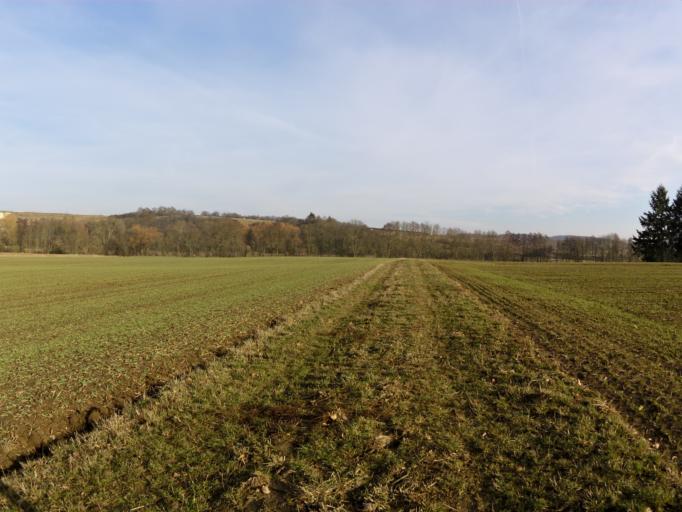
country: DE
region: Bavaria
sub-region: Regierungsbezirk Unterfranken
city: Estenfeld
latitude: 49.8388
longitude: 10.0187
